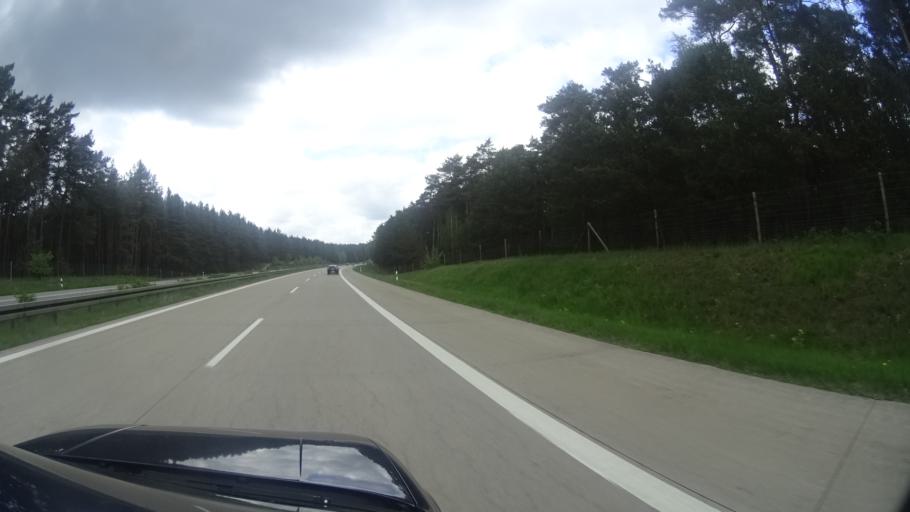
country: DE
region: Mecklenburg-Vorpommern
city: Krakow am See
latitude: 53.5582
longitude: 12.3174
